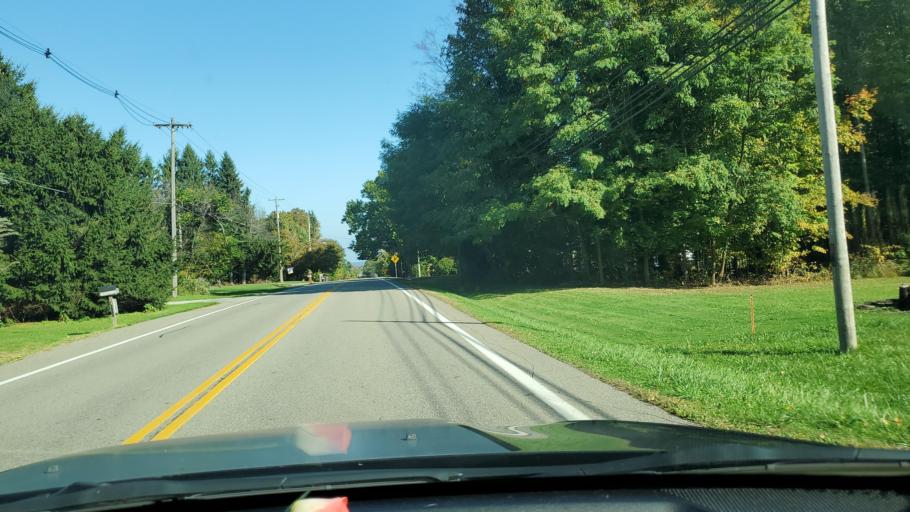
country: US
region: Ohio
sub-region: Trumbull County
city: Brookfield Center
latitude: 41.3445
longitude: -80.5695
